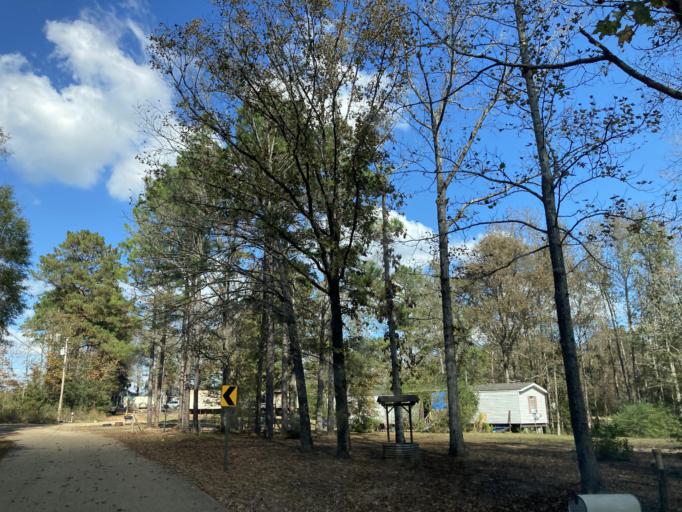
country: US
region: Mississippi
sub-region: Lamar County
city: Sumrall
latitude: 31.3521
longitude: -89.5440
